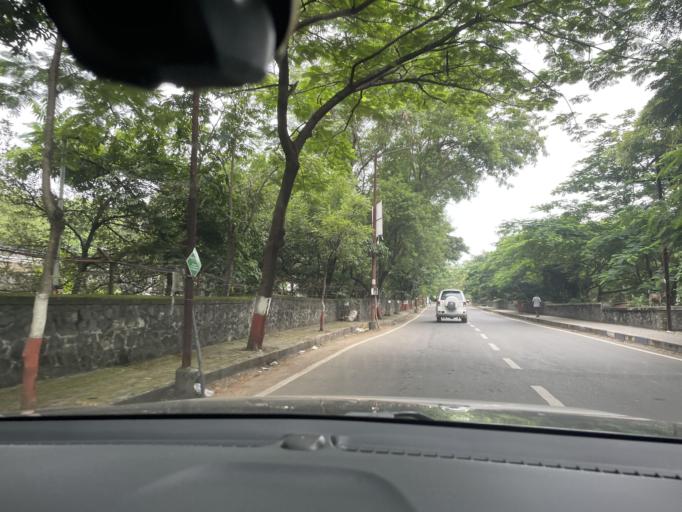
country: IN
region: Maharashtra
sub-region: Pune Division
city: Shivaji Nagar
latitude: 18.5385
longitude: 73.8095
